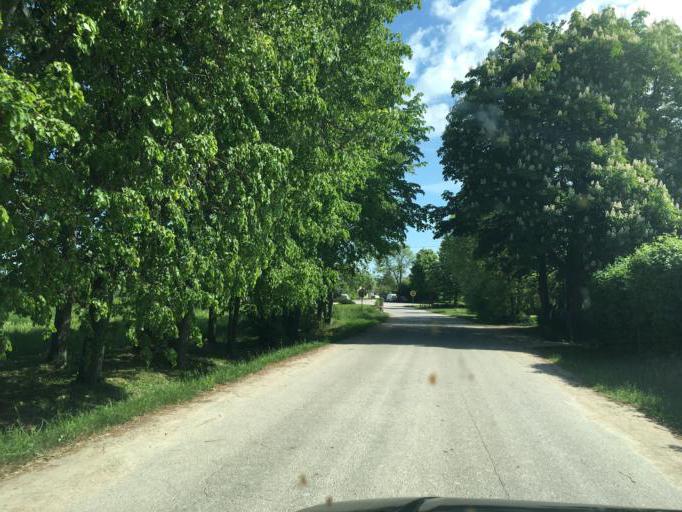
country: LV
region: Talsu Rajons
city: Valdemarpils
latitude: 57.3432
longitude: 22.4921
